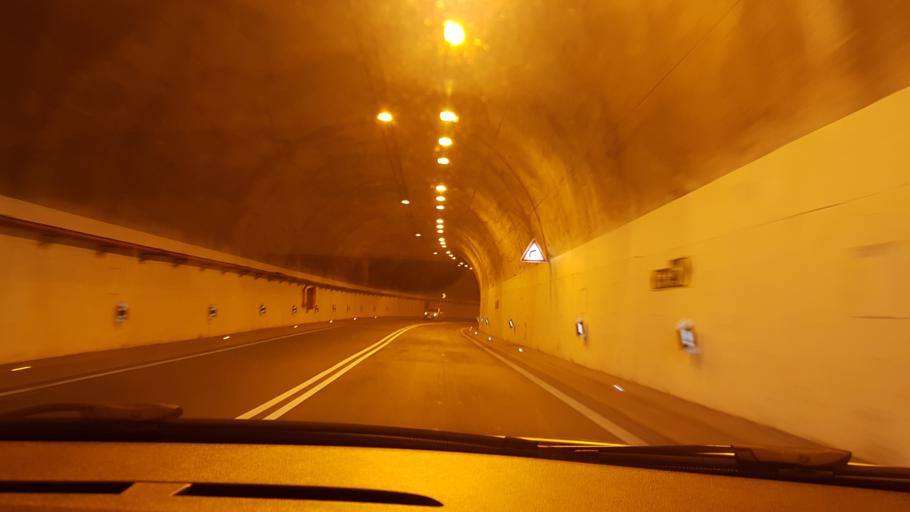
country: PT
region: Madeira
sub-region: Santana
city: Santana
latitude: 32.8185
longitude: -16.8911
